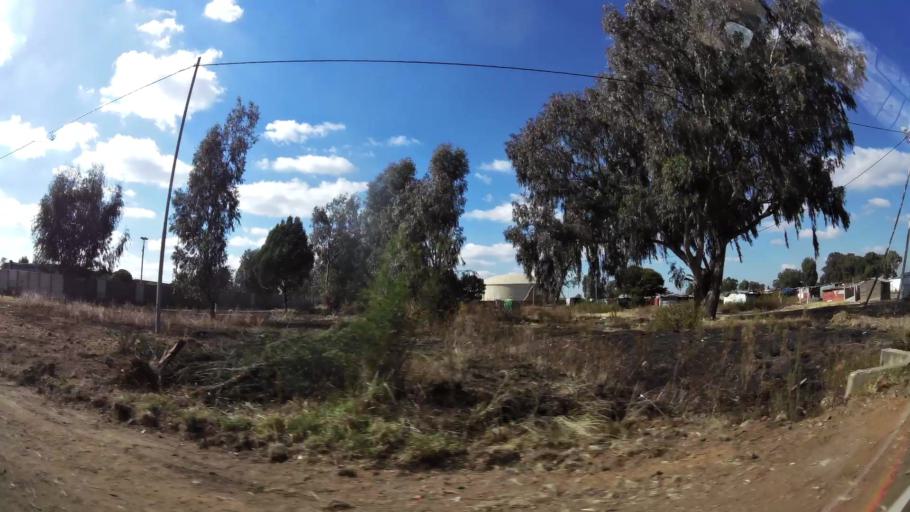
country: ZA
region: Gauteng
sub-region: West Rand District Municipality
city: Krugersdorp
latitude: -26.1301
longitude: 27.8017
